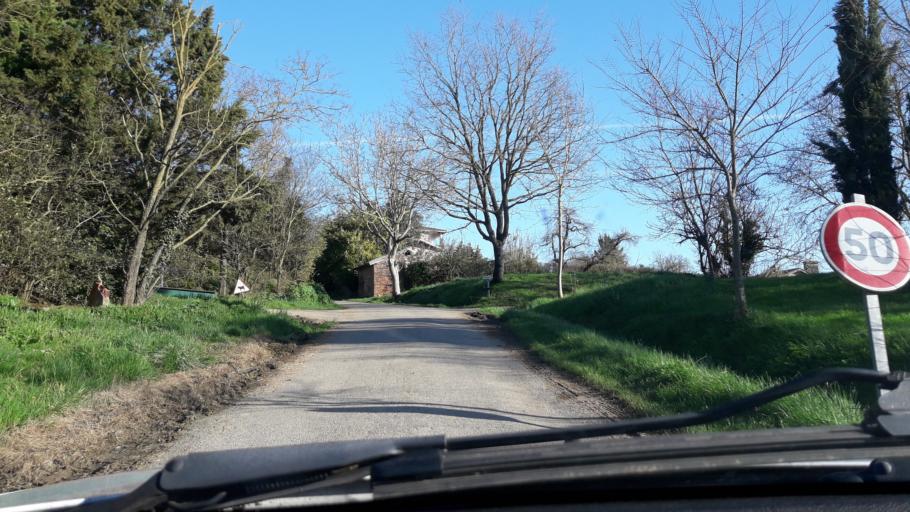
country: FR
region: Midi-Pyrenees
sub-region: Departement du Gers
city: Gimont
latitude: 43.5989
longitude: 0.9766
